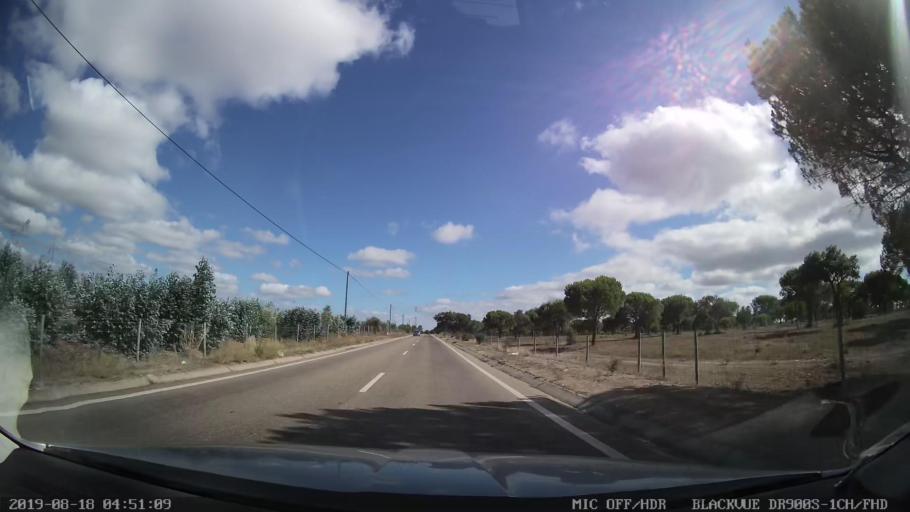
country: PT
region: Santarem
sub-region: Benavente
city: Benavente
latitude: 38.9271
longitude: -8.7769
